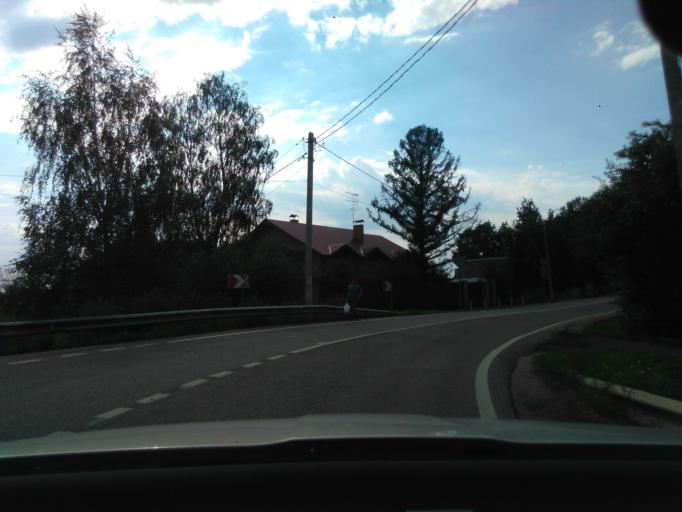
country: RU
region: Moskovskaya
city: Solnechnogorsk
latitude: 56.1411
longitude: 36.8877
